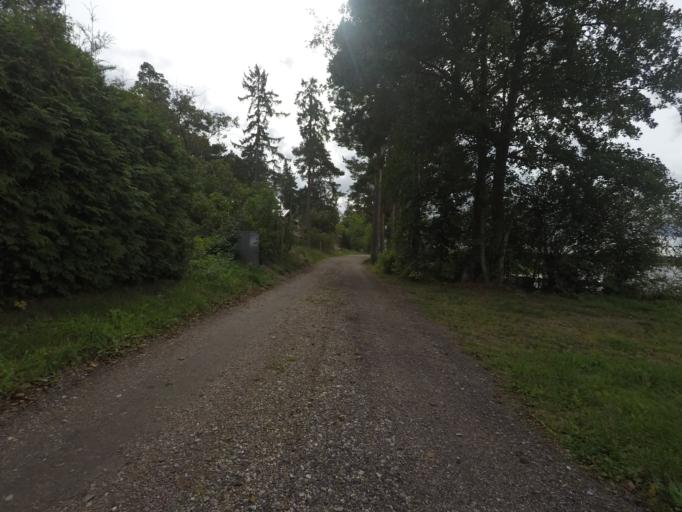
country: SE
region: Vaestmanland
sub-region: Kungsors Kommun
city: Kungsoer
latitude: 59.4680
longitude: 16.0716
